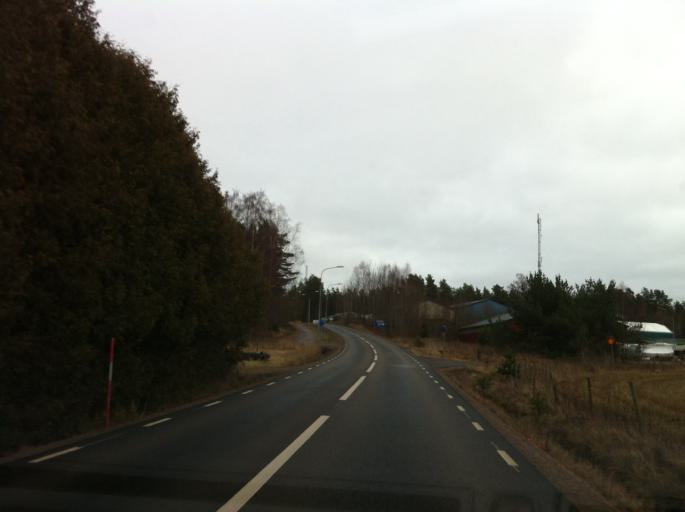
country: SE
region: Kalmar
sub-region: Vasterviks Kommun
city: Overum
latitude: 57.9074
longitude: 16.2341
